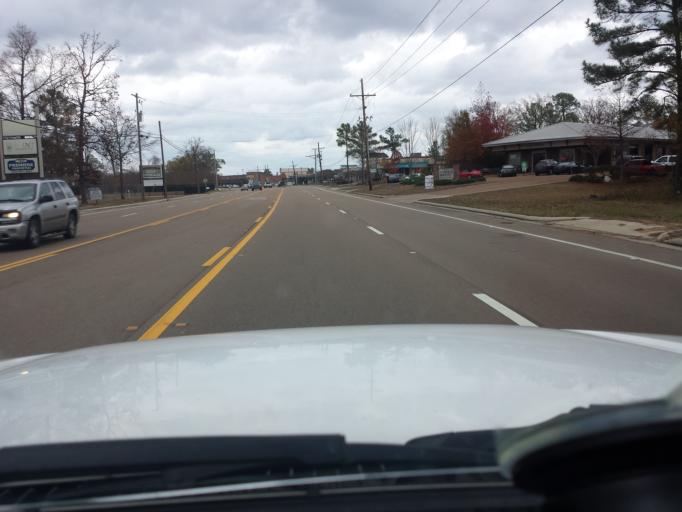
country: US
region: Mississippi
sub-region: Madison County
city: Ridgeland
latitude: 32.3769
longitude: -90.0444
